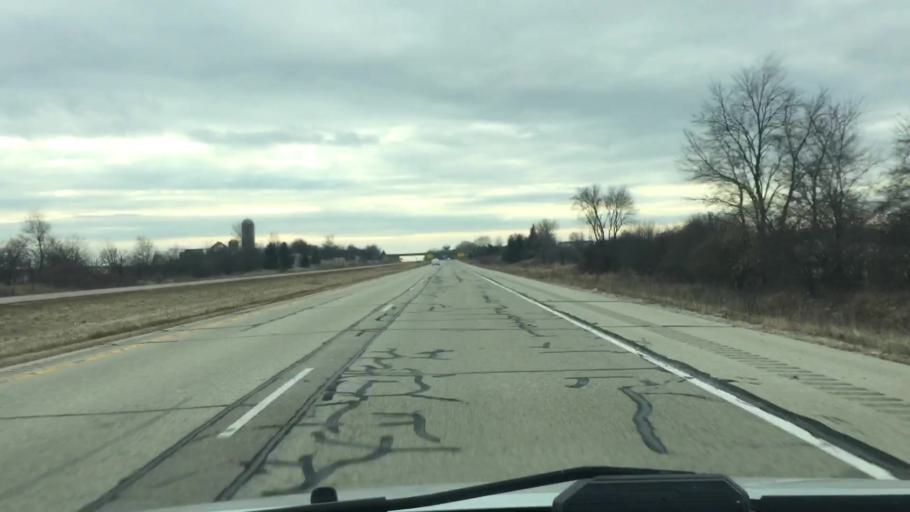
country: US
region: Wisconsin
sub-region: Walworth County
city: Genoa City
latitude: 42.5232
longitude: -88.3163
